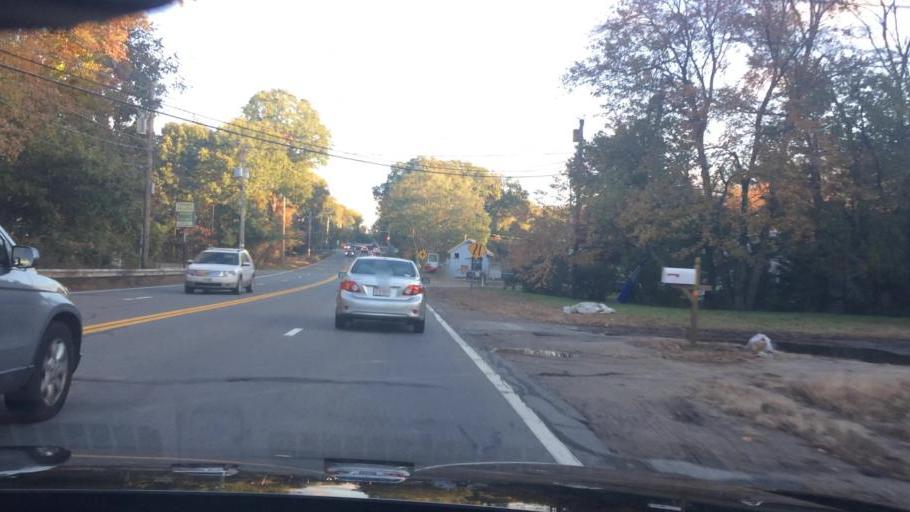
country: US
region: Massachusetts
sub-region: Middlesex County
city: Chelmsford
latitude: 42.6285
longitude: -71.3714
